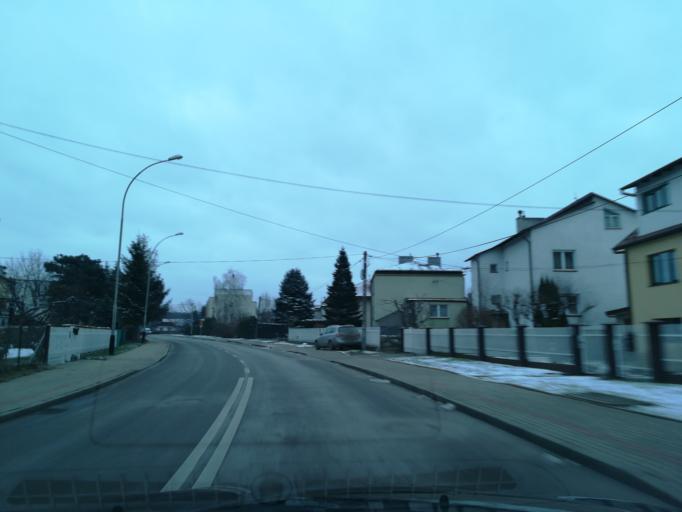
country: PL
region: Subcarpathian Voivodeship
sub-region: Rzeszow
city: Rzeszow
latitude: 50.0284
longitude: 22.0278
